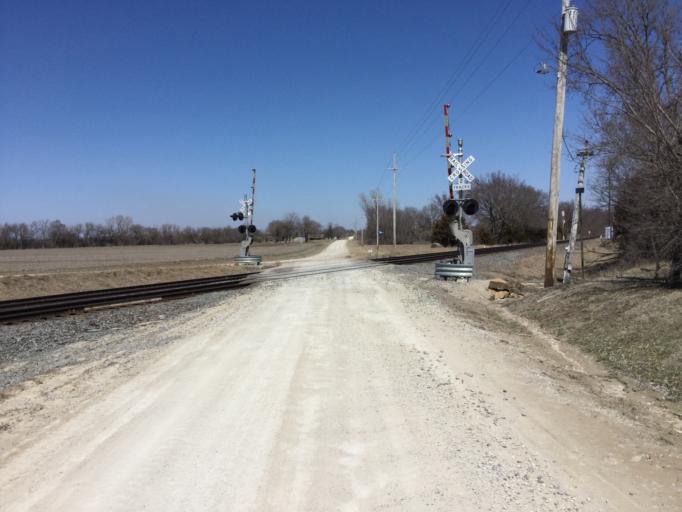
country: US
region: Kansas
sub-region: Anderson County
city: Garnett
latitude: 38.2461
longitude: -95.2778
